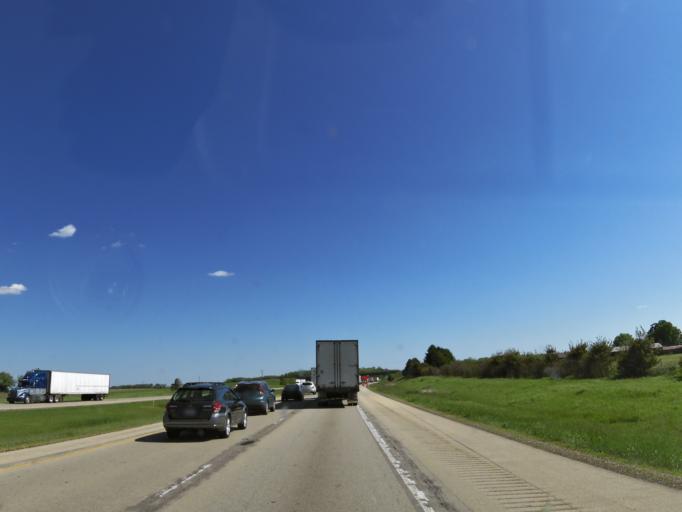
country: US
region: Illinois
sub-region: Ogle County
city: Davis Junction
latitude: 42.0610
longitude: -89.0201
